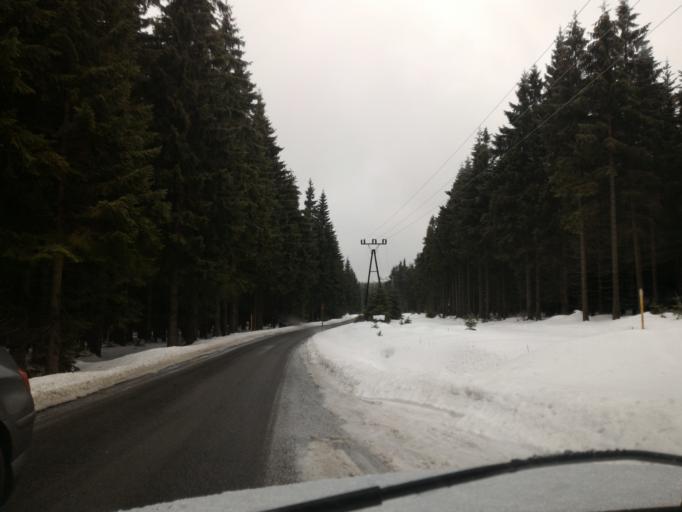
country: CZ
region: Liberecky
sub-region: Okres Jablonec nad Nisou
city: Korenov
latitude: 50.8040
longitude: 15.3524
